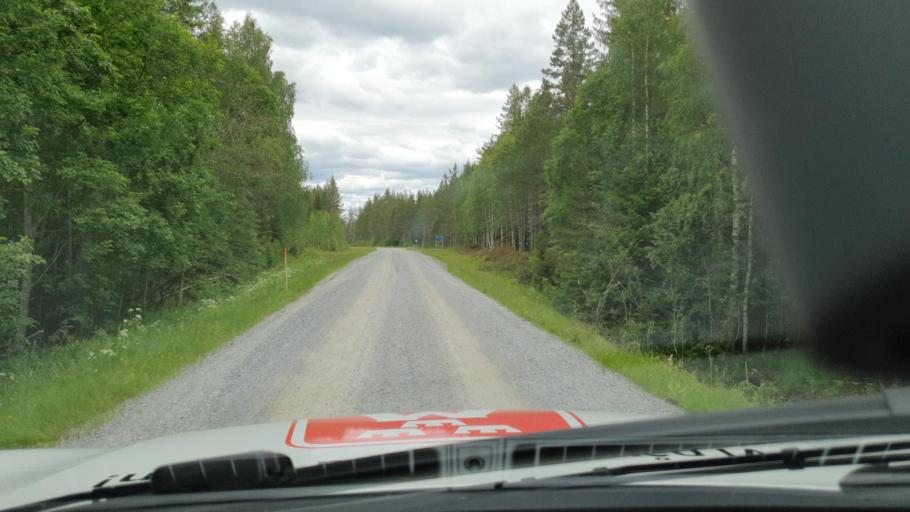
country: SE
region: Vaesterbotten
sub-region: Nordmalings Kommun
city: Nordmaling
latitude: 63.7237
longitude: 19.4307
